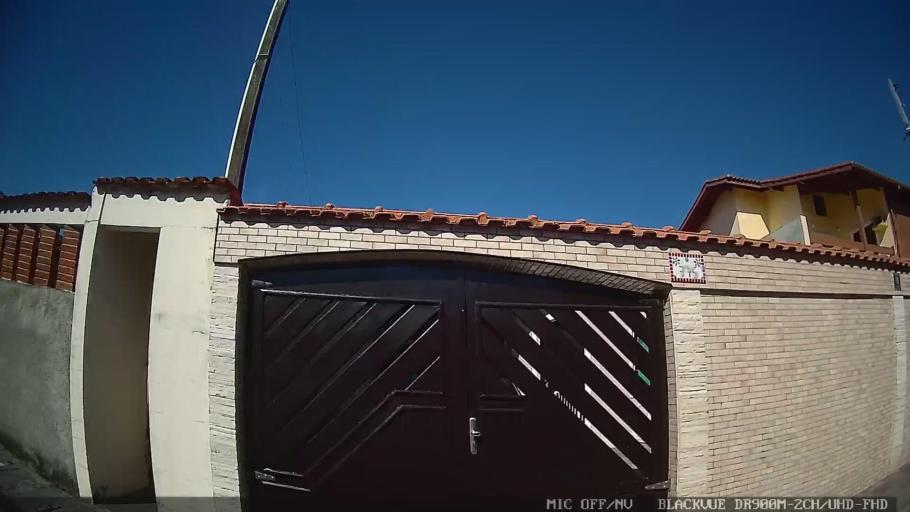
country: BR
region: Sao Paulo
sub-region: Peruibe
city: Peruibe
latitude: -24.2788
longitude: -46.9460
